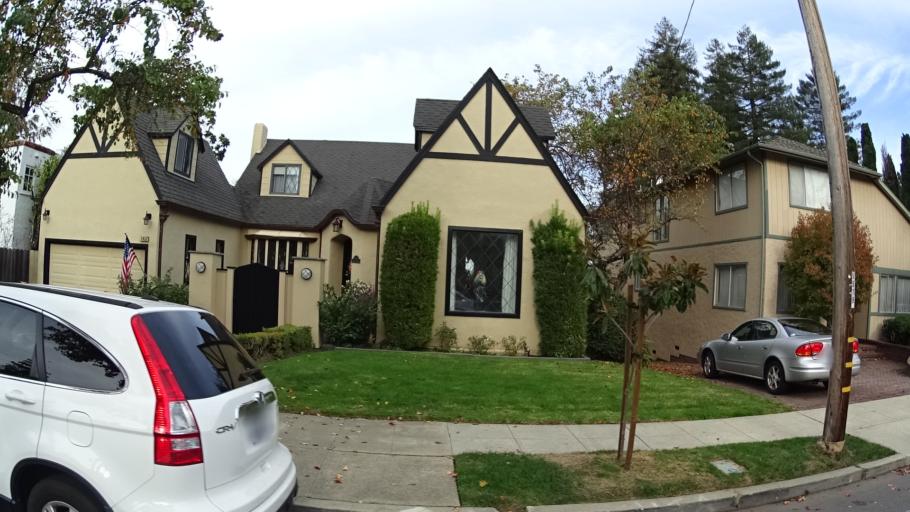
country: US
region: California
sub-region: San Mateo County
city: Hillsborough
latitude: 37.5804
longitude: -122.3812
